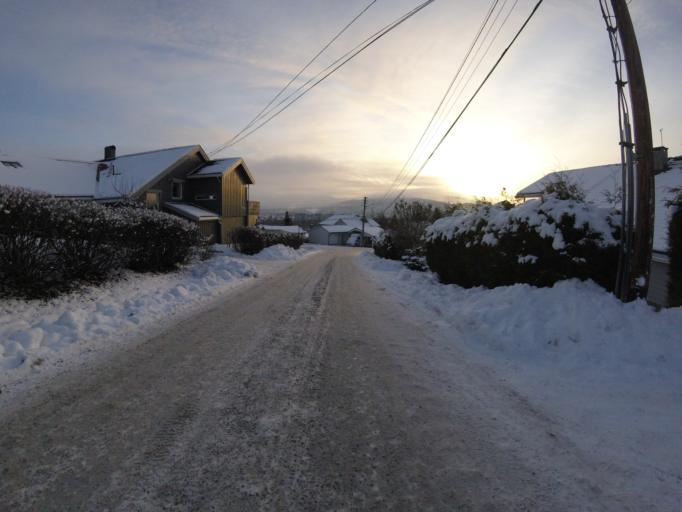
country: NO
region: Akershus
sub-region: Skedsmo
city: Lillestrom
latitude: 59.9659
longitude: 11.0611
